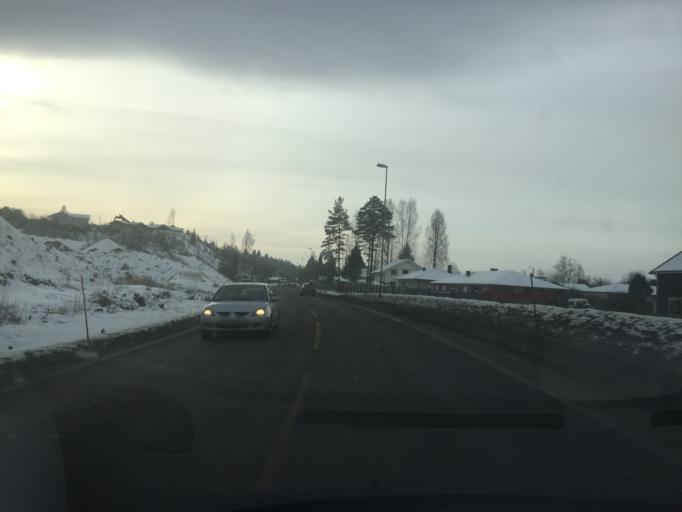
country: NO
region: Hedmark
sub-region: Elverum
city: Elverum
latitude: 60.8931
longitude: 11.5754
